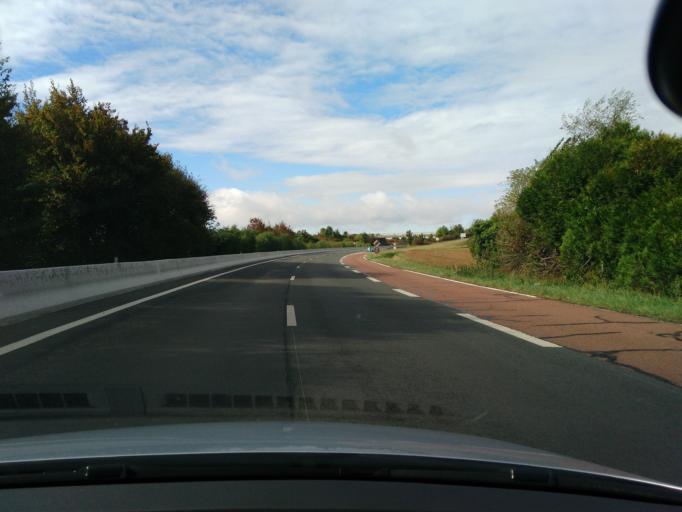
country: FR
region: Centre
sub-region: Departement d'Eure-et-Loir
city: Bu
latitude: 48.7609
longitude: 1.5189
